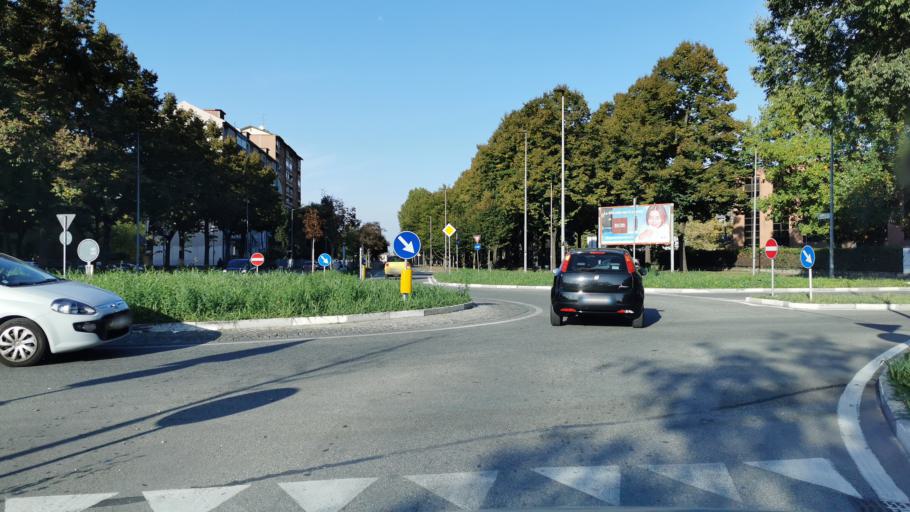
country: IT
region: Piedmont
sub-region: Provincia di Torino
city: Turin
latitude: 45.0948
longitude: 7.7085
